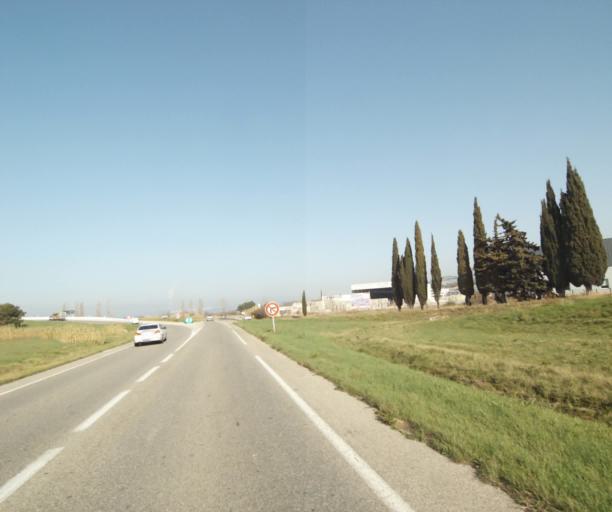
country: FR
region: Provence-Alpes-Cote d'Azur
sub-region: Departement des Bouches-du-Rhone
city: Vitrolles
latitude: 43.4449
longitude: 5.2313
